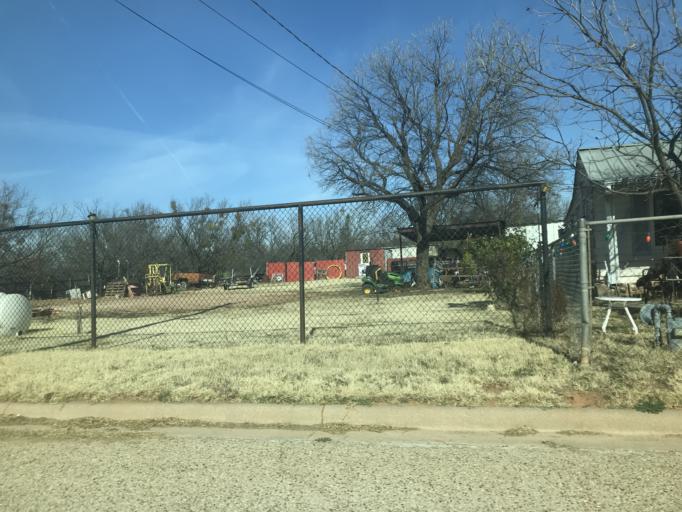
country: US
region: Texas
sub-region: Taylor County
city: Abilene
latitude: 32.4996
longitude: -99.7425
